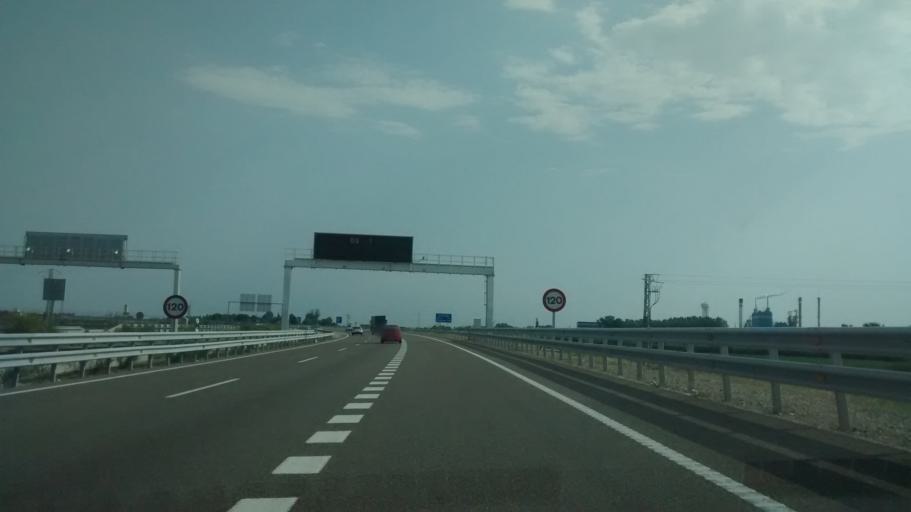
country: ES
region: Aragon
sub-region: Provincia de Zaragoza
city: Zaragoza
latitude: 41.6843
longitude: -0.8329
